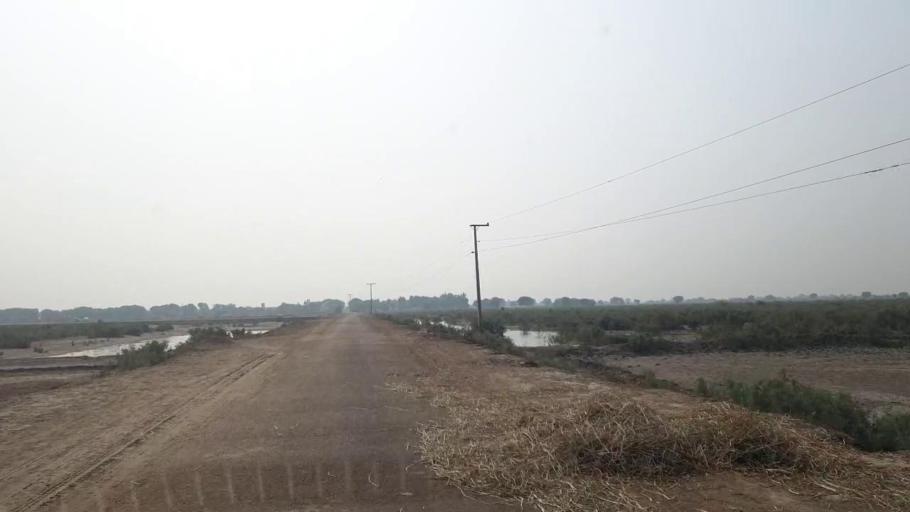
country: PK
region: Sindh
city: Matli
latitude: 25.1321
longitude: 68.6906
